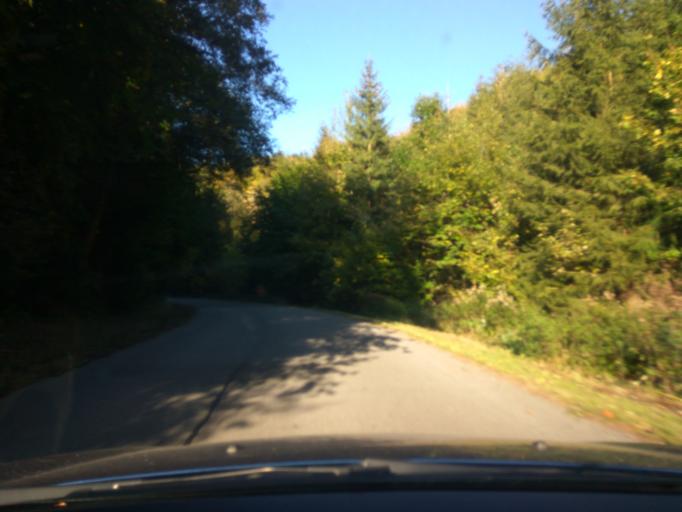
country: SK
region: Banskobystricky
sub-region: Okres Ziar nad Hronom
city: Kremnica
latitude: 48.7206
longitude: 18.9665
